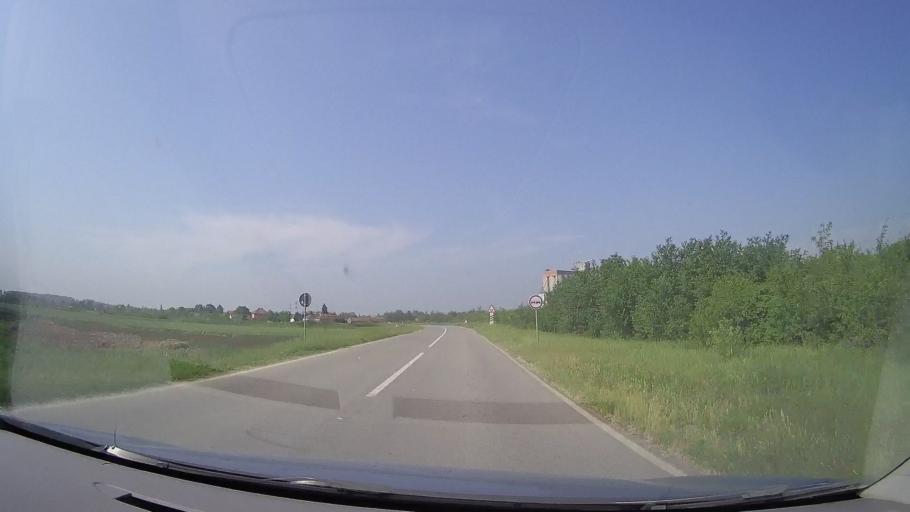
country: RS
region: Autonomna Pokrajina Vojvodina
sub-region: Srednjebanatski Okrug
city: Secanj
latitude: 45.3761
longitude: 20.7802
